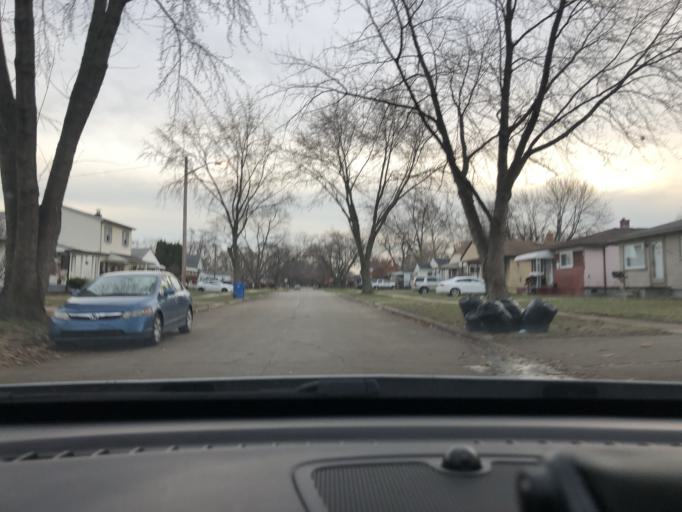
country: US
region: Michigan
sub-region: Wayne County
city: Allen Park
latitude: 42.2767
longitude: -83.2229
